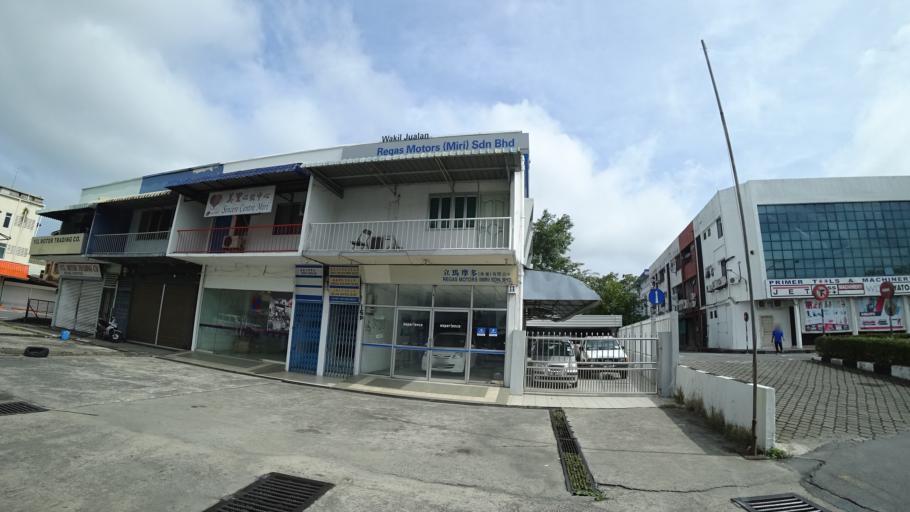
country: MY
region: Sarawak
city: Miri
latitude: 4.3967
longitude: 113.9905
